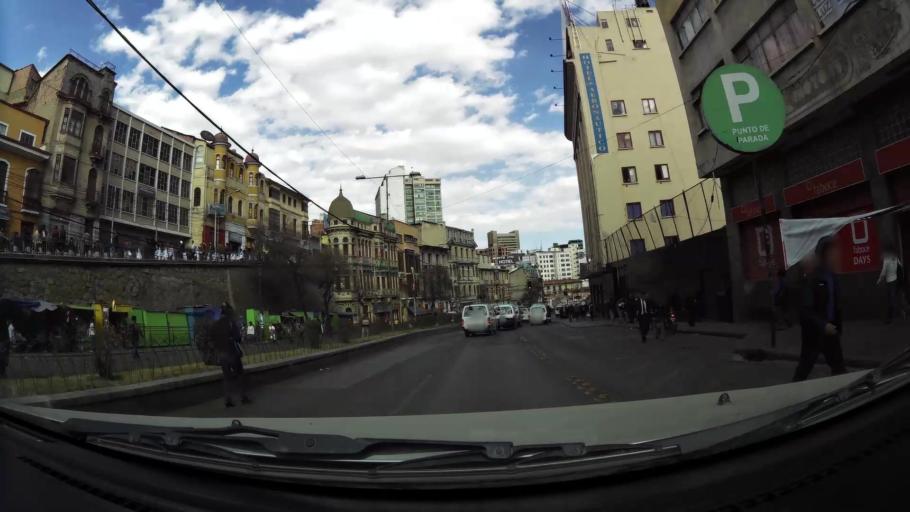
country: BO
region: La Paz
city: La Paz
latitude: -16.4925
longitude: -68.1377
